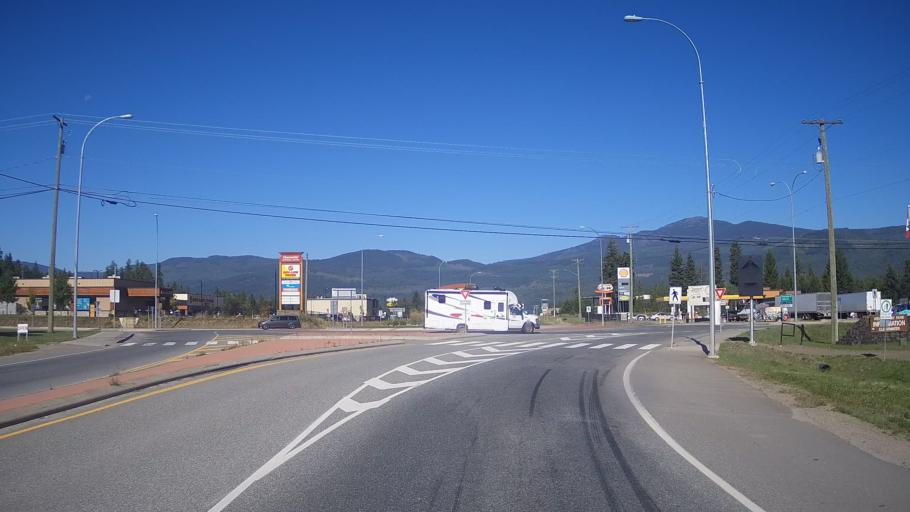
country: CA
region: British Columbia
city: Chase
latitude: 51.6509
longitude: -120.0374
